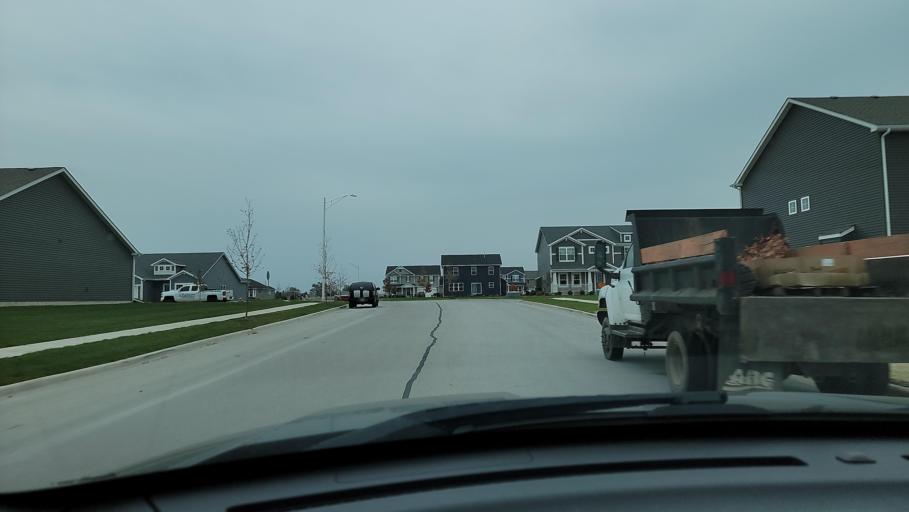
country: US
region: Indiana
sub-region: Porter County
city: Portage
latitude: 41.5453
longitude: -87.1715
